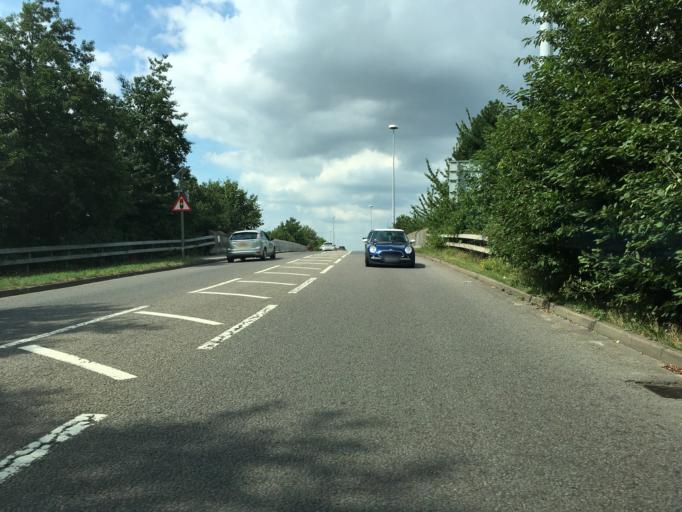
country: GB
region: England
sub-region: Gloucestershire
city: Barnwood
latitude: 51.8588
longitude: -2.2221
